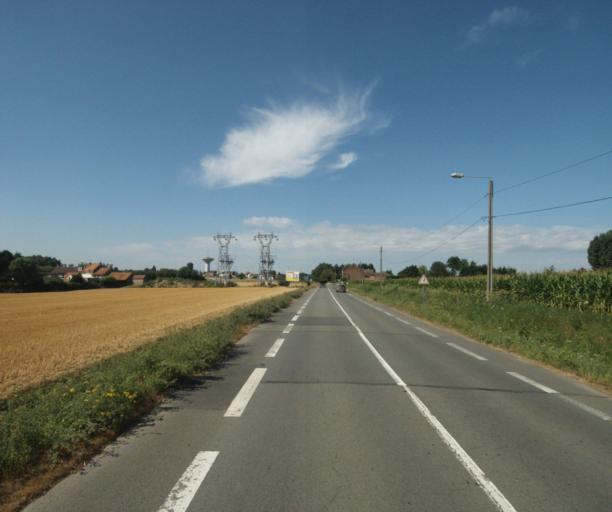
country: FR
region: Nord-Pas-de-Calais
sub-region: Departement du Nord
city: Roncq
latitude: 50.7719
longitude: 3.1083
